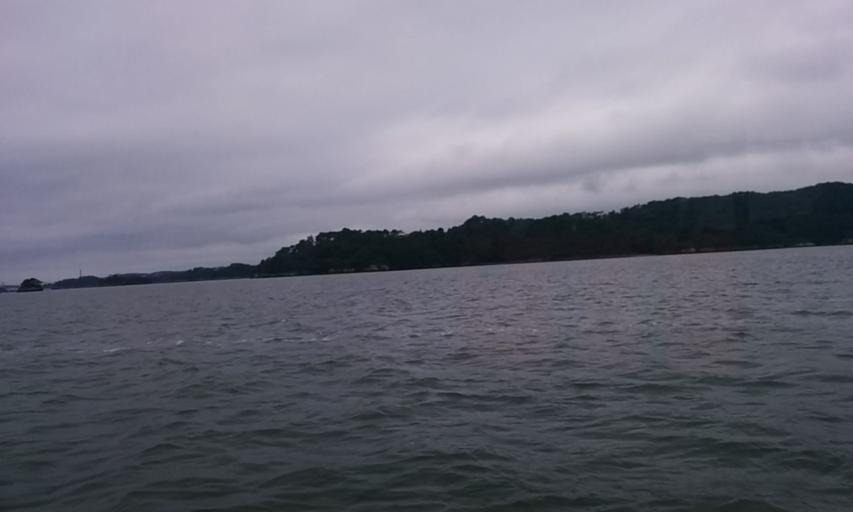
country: JP
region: Miyagi
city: Matsushima
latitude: 38.3541
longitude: 141.0732
